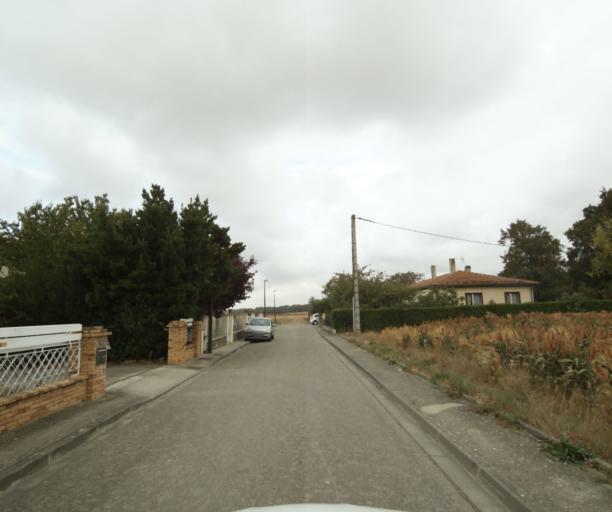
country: FR
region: Midi-Pyrenees
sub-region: Departement de la Haute-Garonne
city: Villefranche-de-Lauragais
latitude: 43.4061
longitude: 1.7051
